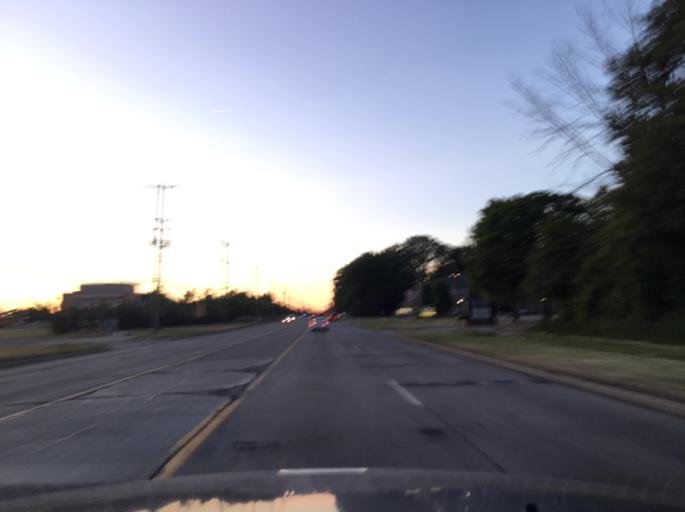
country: US
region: Michigan
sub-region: Macomb County
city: Clinton
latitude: 42.6161
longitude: -82.9530
